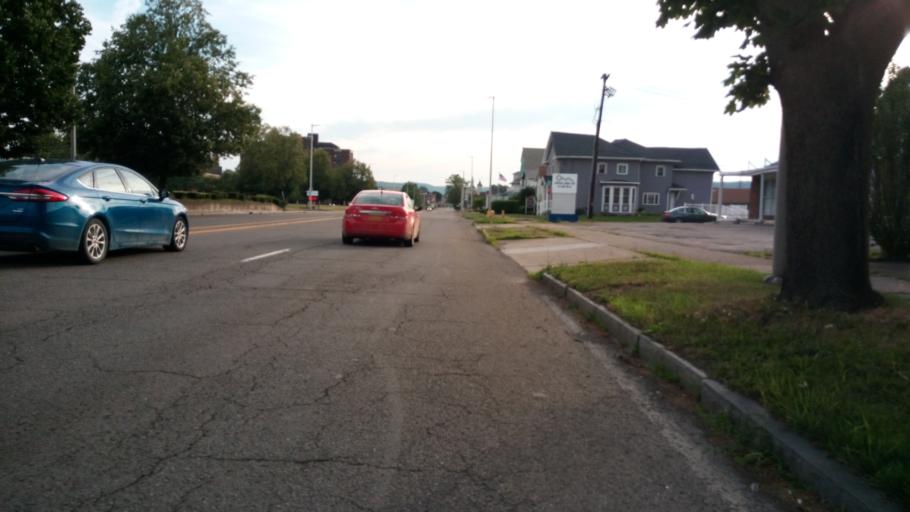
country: US
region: New York
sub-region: Chemung County
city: Elmira
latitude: 42.0940
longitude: -76.7946
